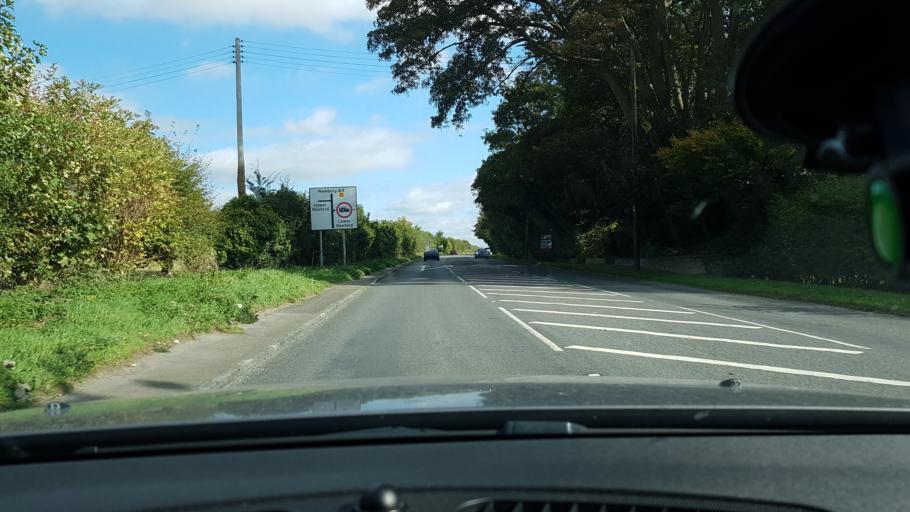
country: GB
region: England
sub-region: West Berkshire
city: Hungerford
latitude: 51.4159
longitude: -1.4964
